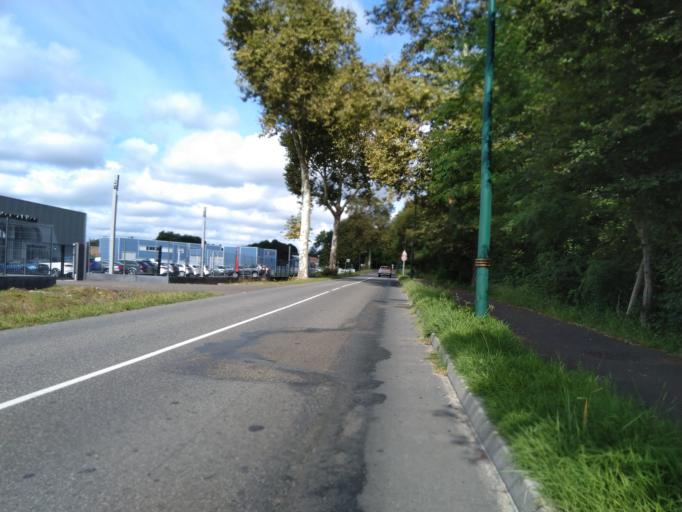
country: FR
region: Aquitaine
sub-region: Departement des Landes
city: Mees
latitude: 43.7288
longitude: -1.0887
